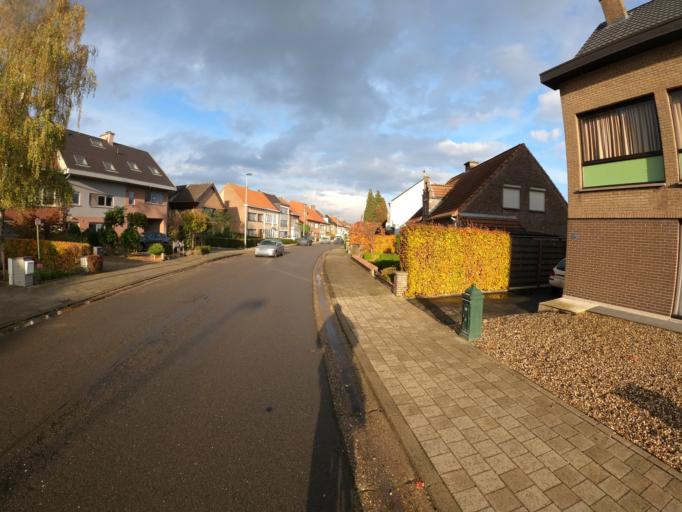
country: BE
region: Flanders
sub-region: Provincie Oost-Vlaanderen
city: Temse
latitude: 51.1249
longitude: 4.1970
